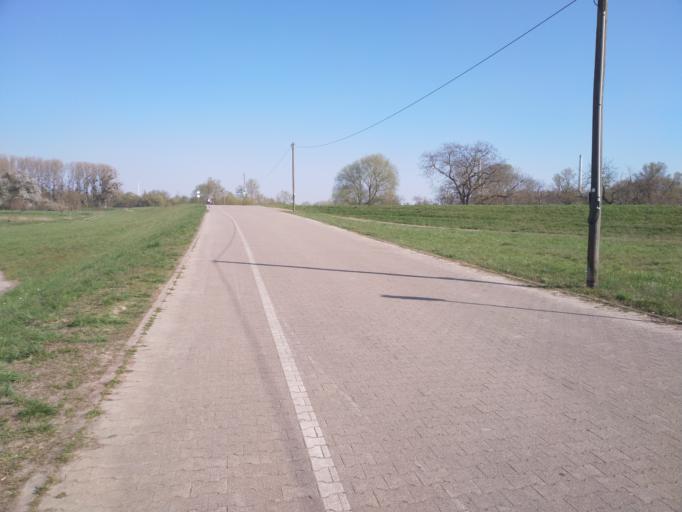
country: DE
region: Rheinland-Pfalz
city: Worth am Rhein
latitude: 49.0266
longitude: 8.2885
